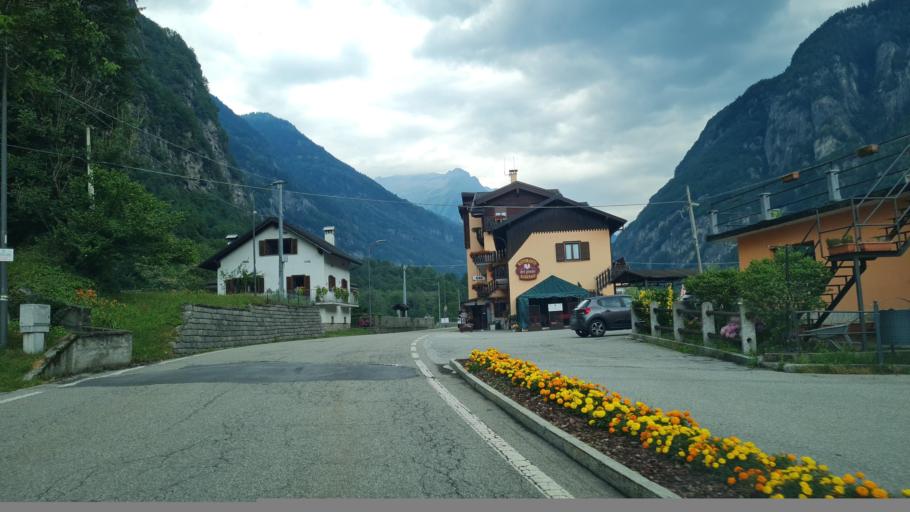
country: IT
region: Piedmont
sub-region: Provincia Verbano-Cusio-Ossola
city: Premia
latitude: 46.2794
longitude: 8.3526
